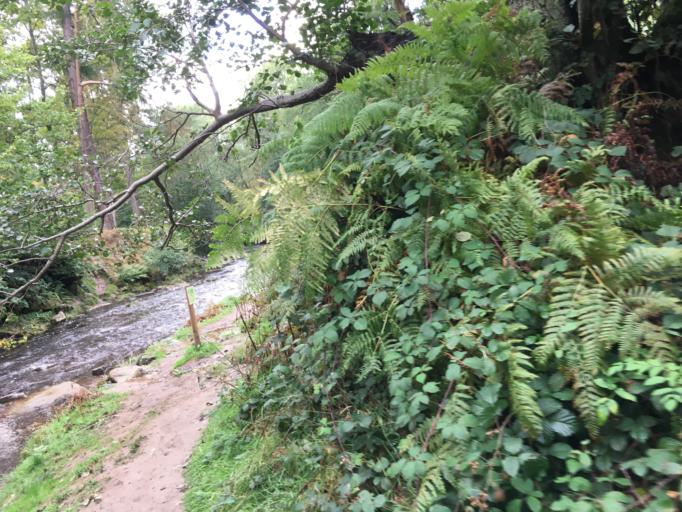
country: GB
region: England
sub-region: North Yorkshire
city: Sleights
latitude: 54.4086
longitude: -0.7317
